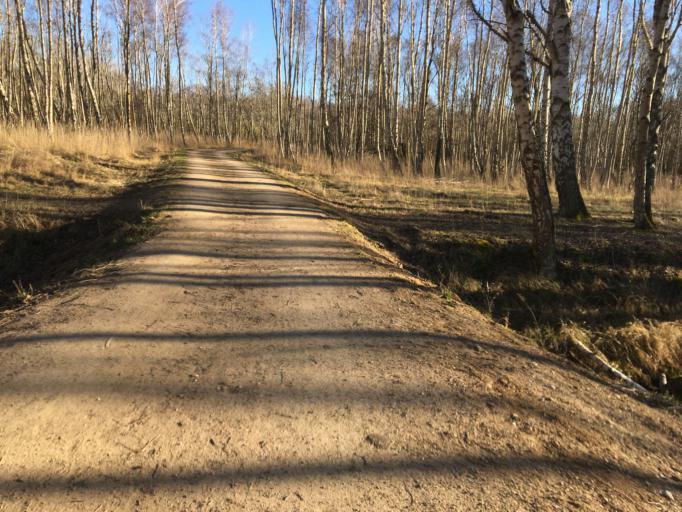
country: DK
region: Capital Region
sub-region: Tarnby Kommune
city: Tarnby
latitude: 55.5900
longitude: 12.5566
